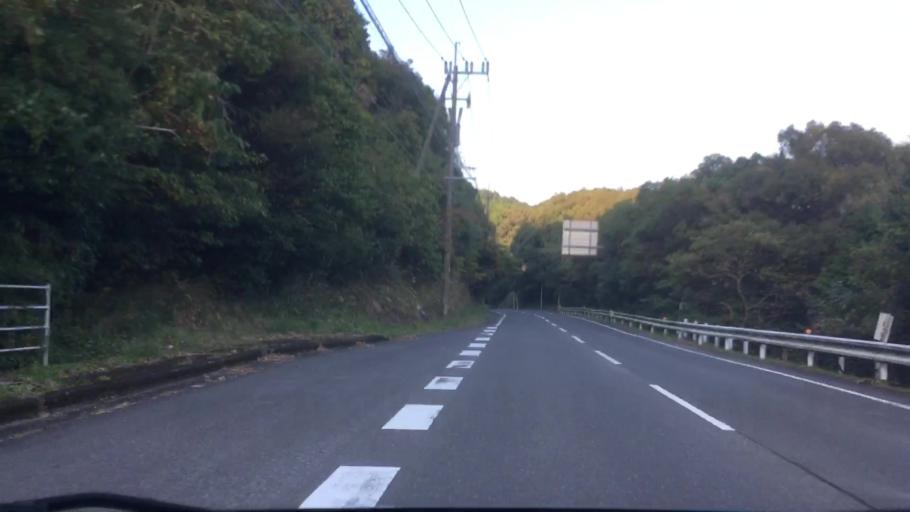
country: JP
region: Nagasaki
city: Sasebo
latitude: 32.9776
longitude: 129.7105
